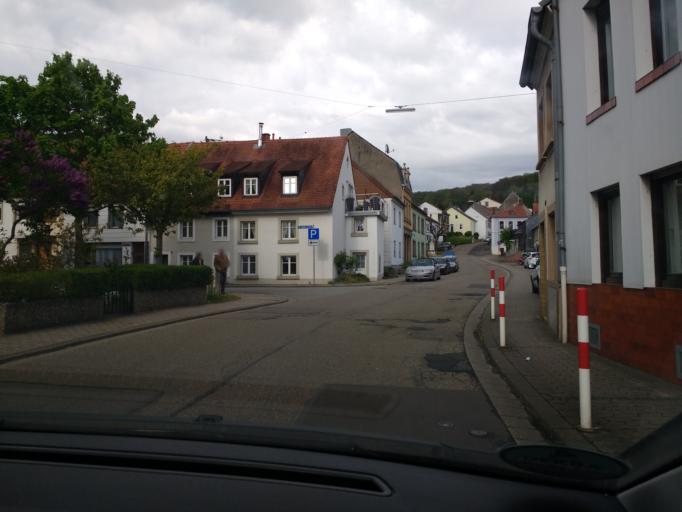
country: DE
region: Saarland
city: Kleinblittersdorf
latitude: 49.1560
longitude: 7.0369
